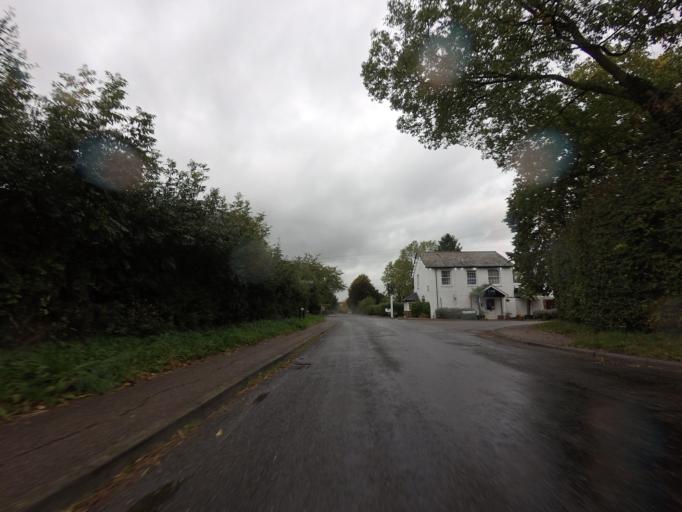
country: GB
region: England
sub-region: Cambridgeshire
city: Comberton
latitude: 52.1626
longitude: -0.0062
